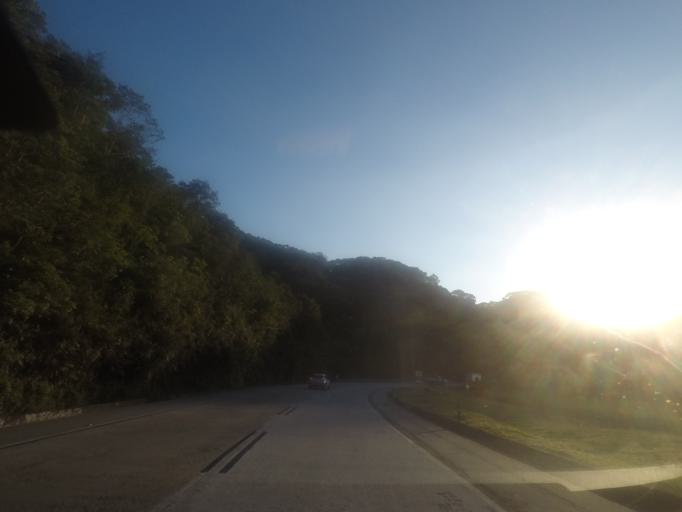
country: BR
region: Rio de Janeiro
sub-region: Petropolis
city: Petropolis
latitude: -22.5215
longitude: -43.2311
